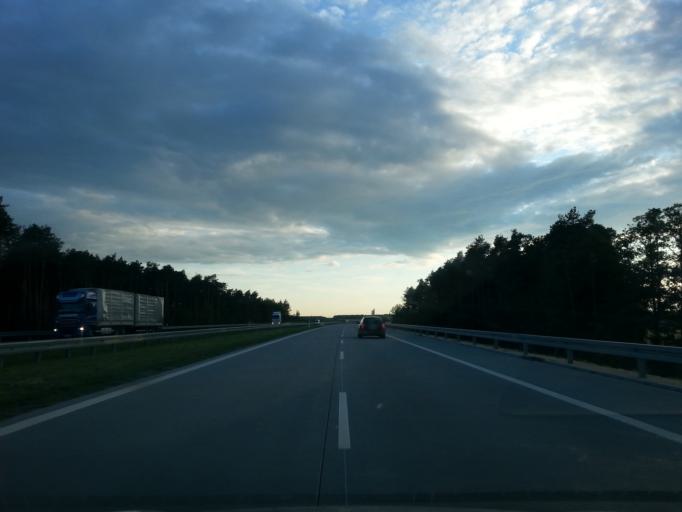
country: PL
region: Lodz Voivodeship
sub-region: Powiat wieruszowski
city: Lututow
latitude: 51.3357
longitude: 18.4786
